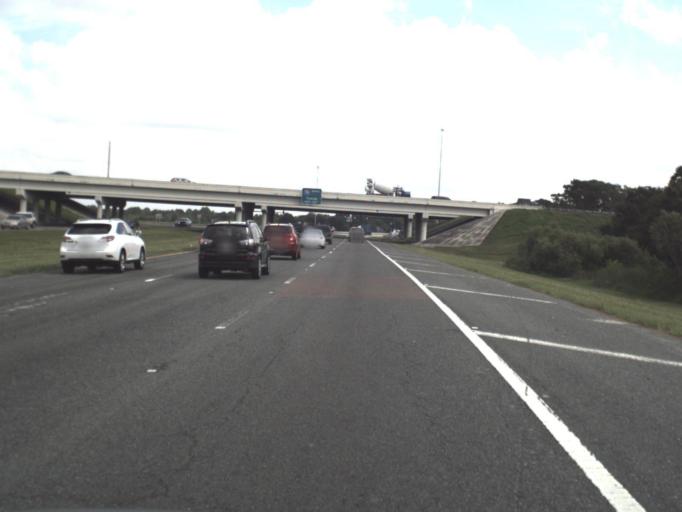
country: US
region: Florida
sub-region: Manatee County
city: Ellenton
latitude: 27.4909
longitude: -82.4740
